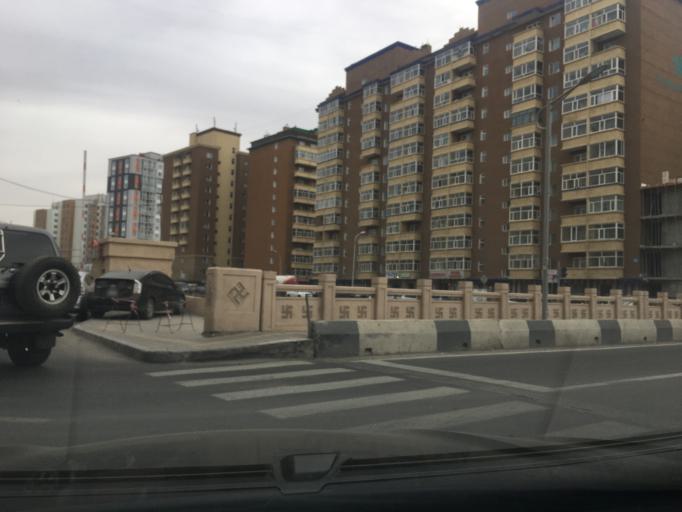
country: MN
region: Ulaanbaatar
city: Ulaanbaatar
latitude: 47.9035
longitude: 106.8829
